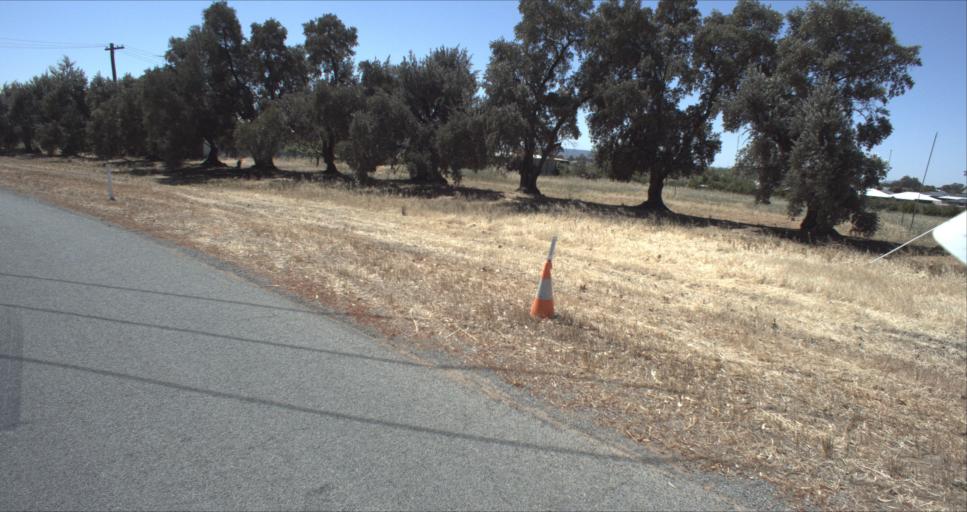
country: AU
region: New South Wales
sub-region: Leeton
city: Leeton
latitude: -34.5400
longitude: 146.3958
